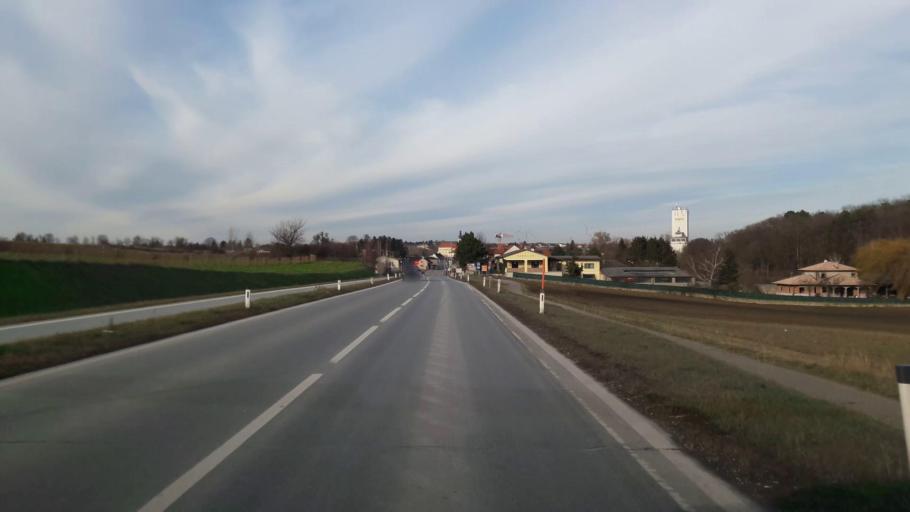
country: AT
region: Lower Austria
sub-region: Politischer Bezirk Mistelbach
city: Gaweinstal
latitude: 48.4683
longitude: 16.5898
